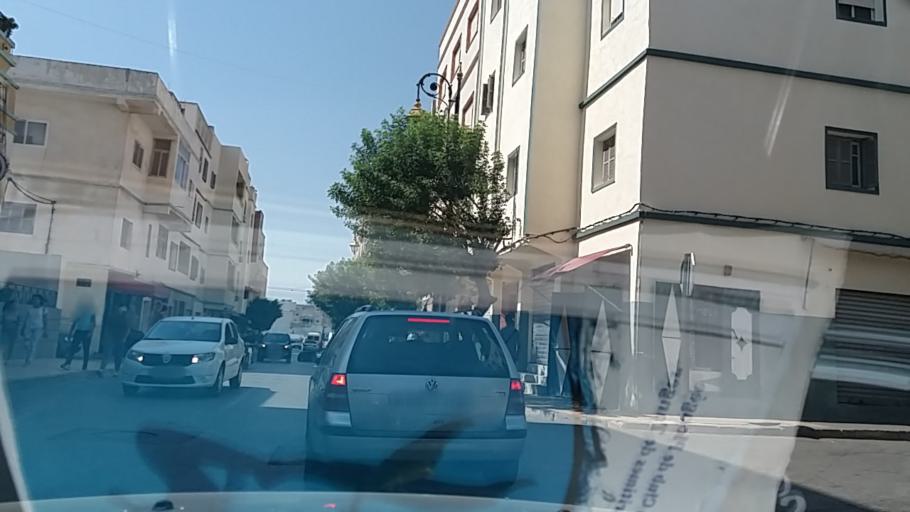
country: MA
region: Tanger-Tetouan
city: Tetouan
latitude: 35.5629
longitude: -5.3673
